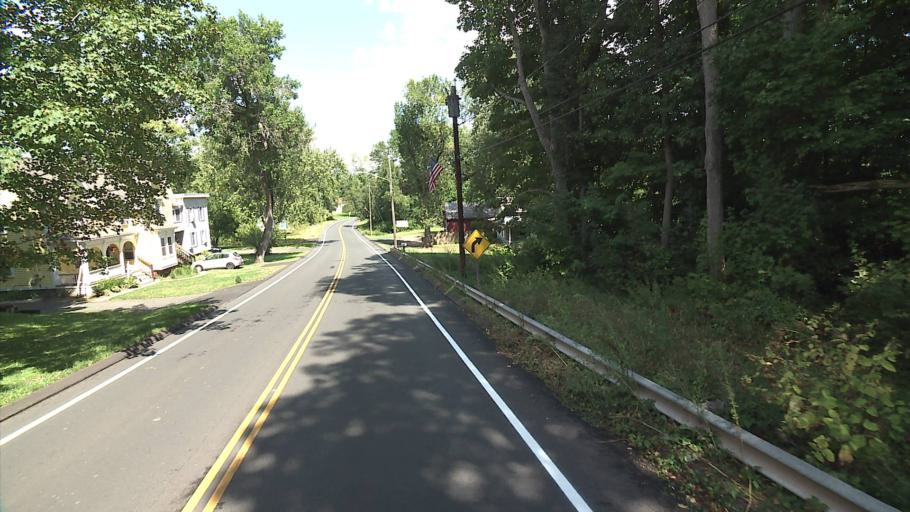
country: US
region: Connecticut
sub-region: Middlesex County
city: Cromwell
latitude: 41.5972
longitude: -72.6206
